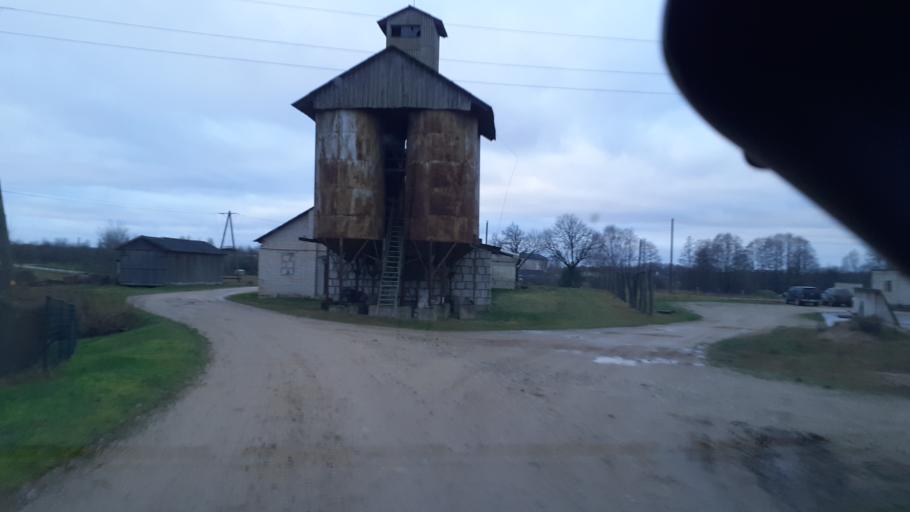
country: LV
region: Alsunga
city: Alsunga
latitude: 56.8882
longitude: 21.6079
